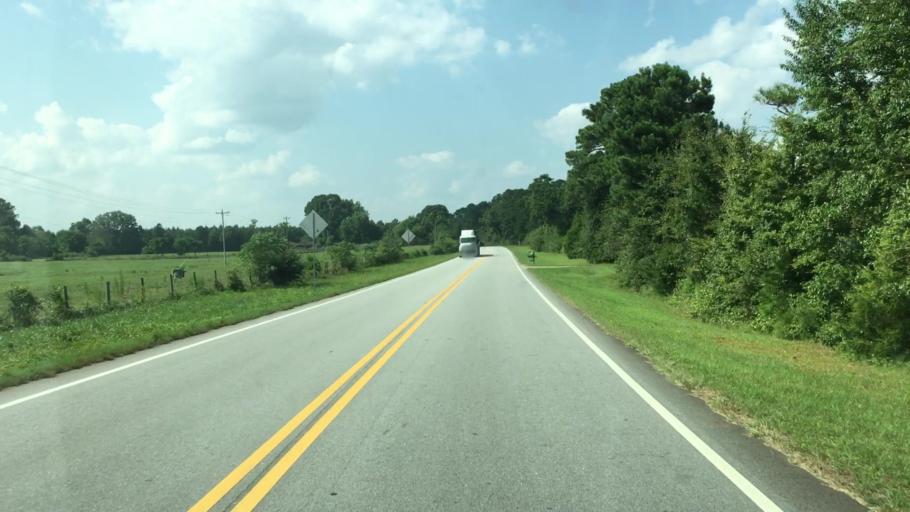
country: US
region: Georgia
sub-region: Jasper County
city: Monticello
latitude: 33.3576
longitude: -83.7497
